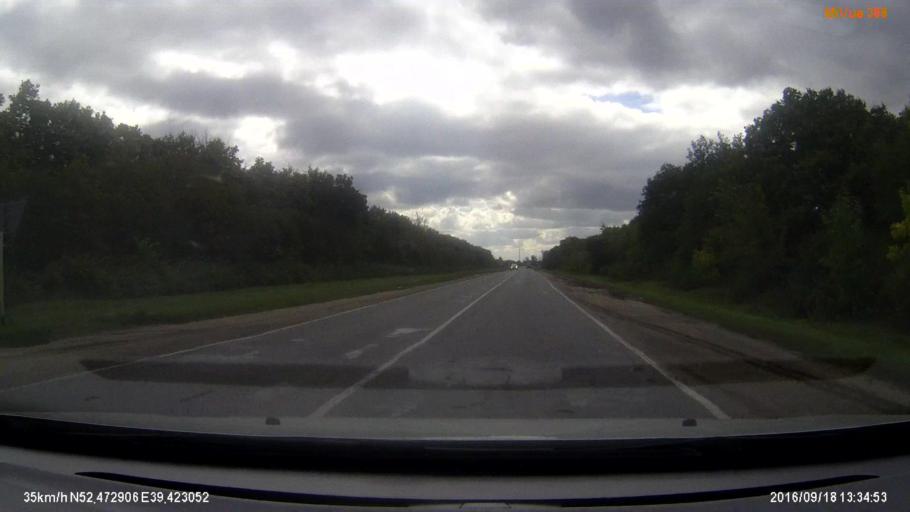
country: RU
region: Lipetsk
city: Borinskoye
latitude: 52.4926
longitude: 39.4475
